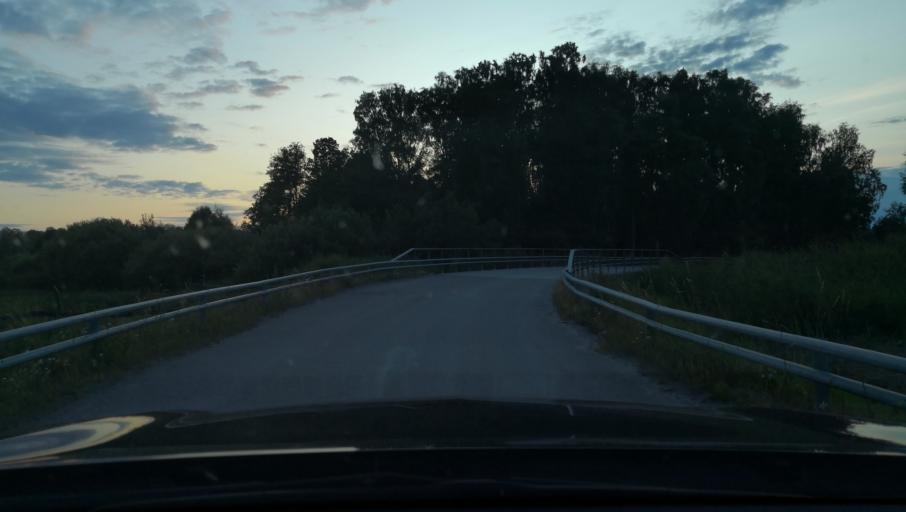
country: SE
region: Uppsala
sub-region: Osthammars Kommun
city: Bjorklinge
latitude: 60.0608
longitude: 17.5810
